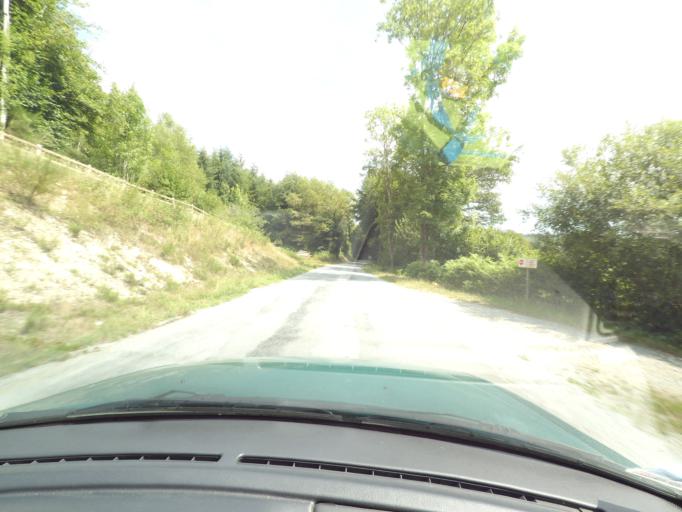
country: FR
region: Limousin
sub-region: Departement de la Correze
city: Bugeat
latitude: 45.7457
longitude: 1.9193
